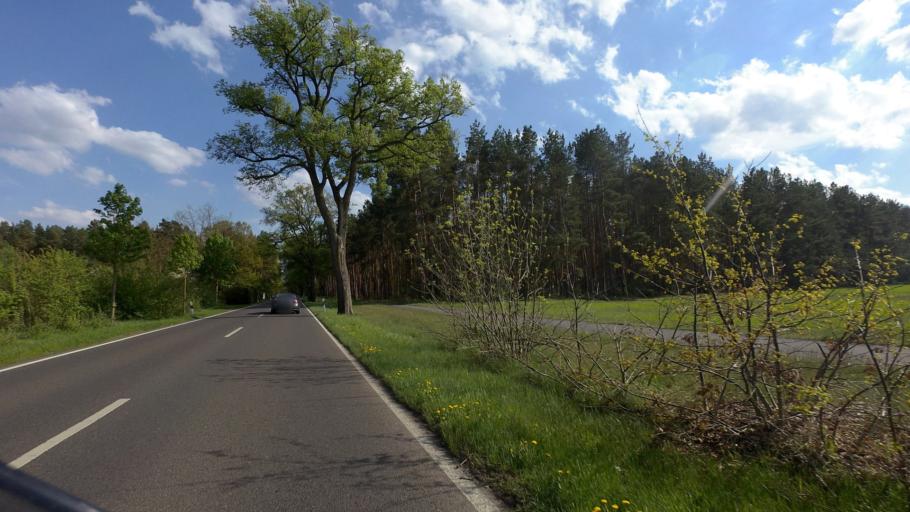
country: DE
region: Brandenburg
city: Zehdenick
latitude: 52.9722
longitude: 13.3565
